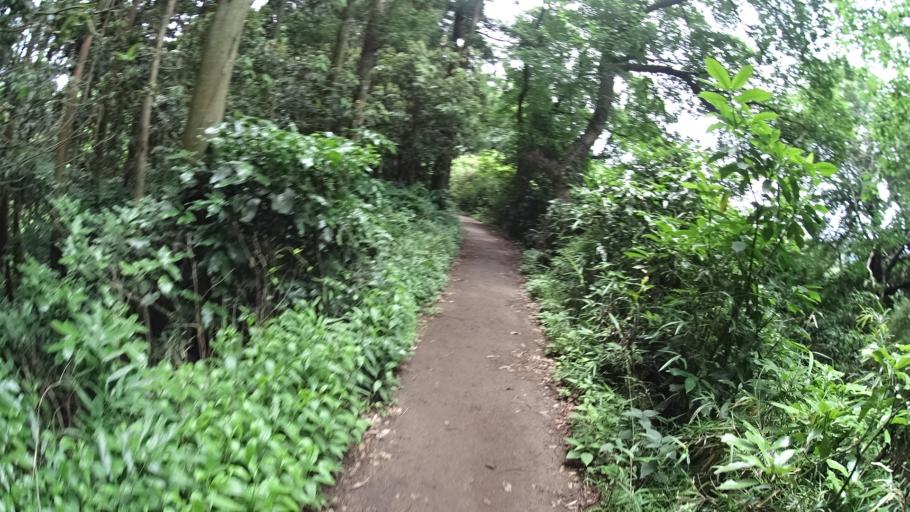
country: JP
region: Kanagawa
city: Zushi
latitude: 35.3373
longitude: 139.5881
